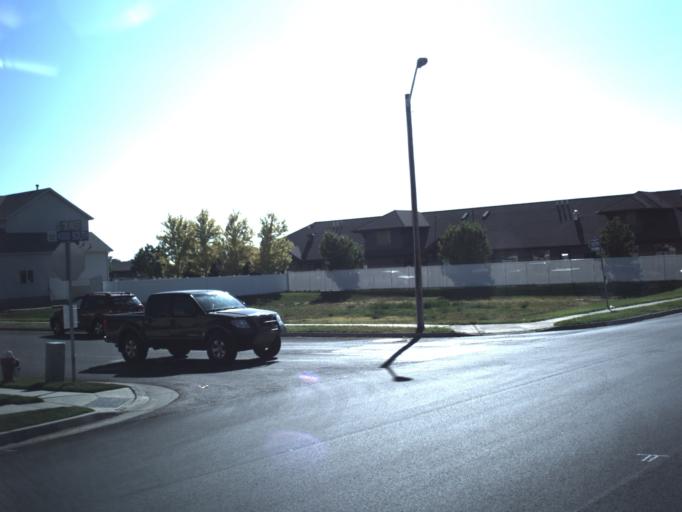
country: US
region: Utah
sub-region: Weber County
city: West Haven
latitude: 41.1906
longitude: -112.0457
